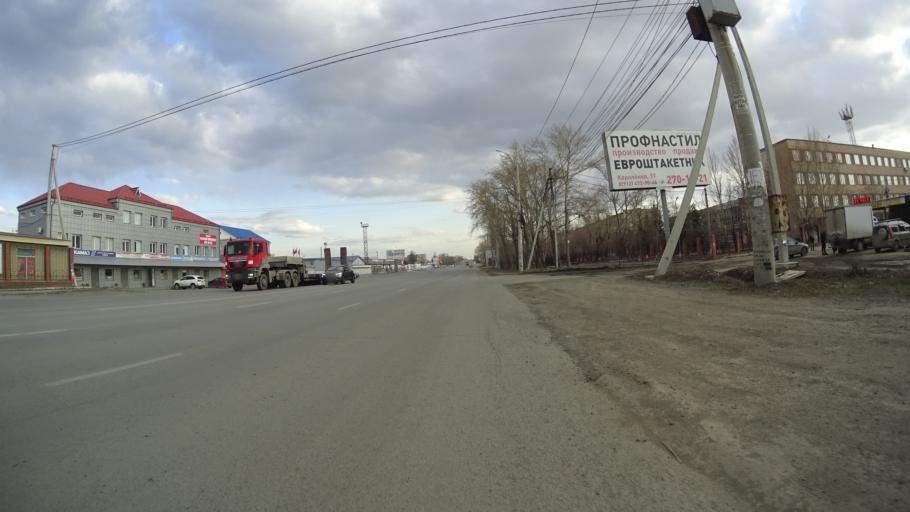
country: RU
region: Chelyabinsk
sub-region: Gorod Chelyabinsk
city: Chelyabinsk
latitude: 55.1096
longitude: 61.3868
